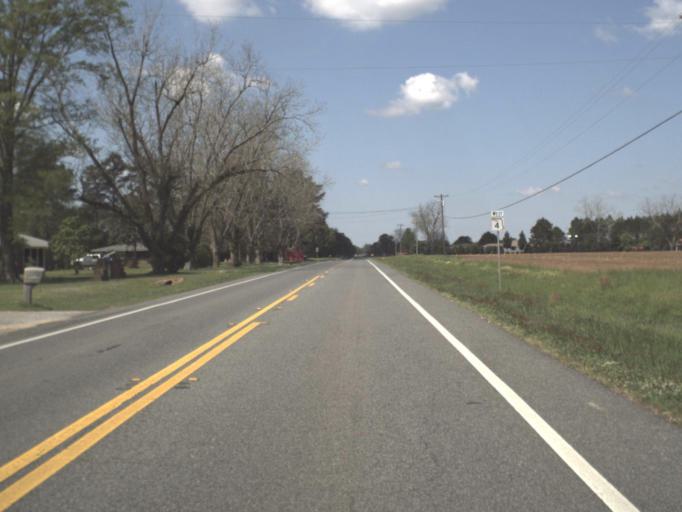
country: US
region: Florida
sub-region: Escambia County
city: Century
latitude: 30.9523
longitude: -87.1224
